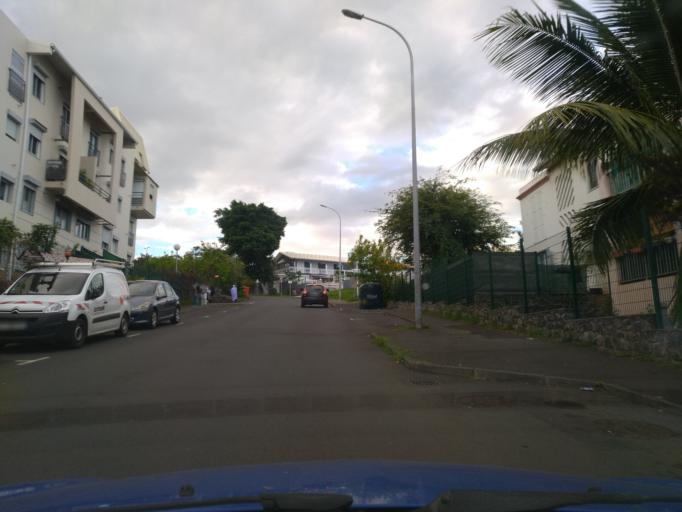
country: RE
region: Reunion
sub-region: Reunion
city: Saint-Pierre
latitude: -21.3318
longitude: 55.4742
